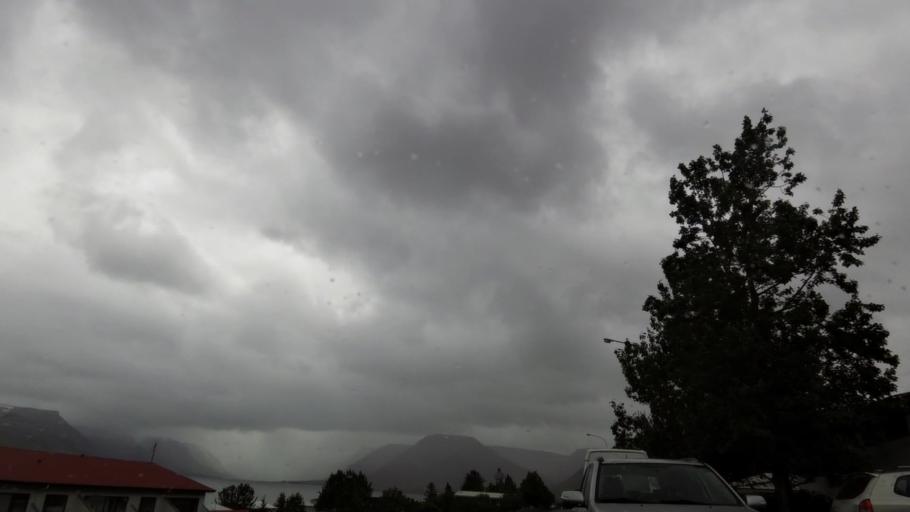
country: IS
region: Westfjords
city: Isafjoerdur
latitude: 65.8730
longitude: -23.4856
